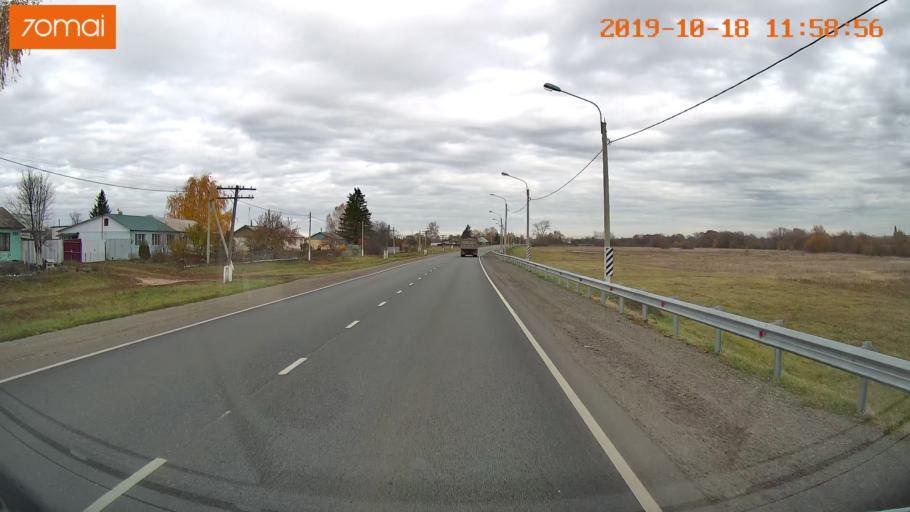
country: RU
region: Rjazan
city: Zakharovo
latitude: 54.2769
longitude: 39.1710
